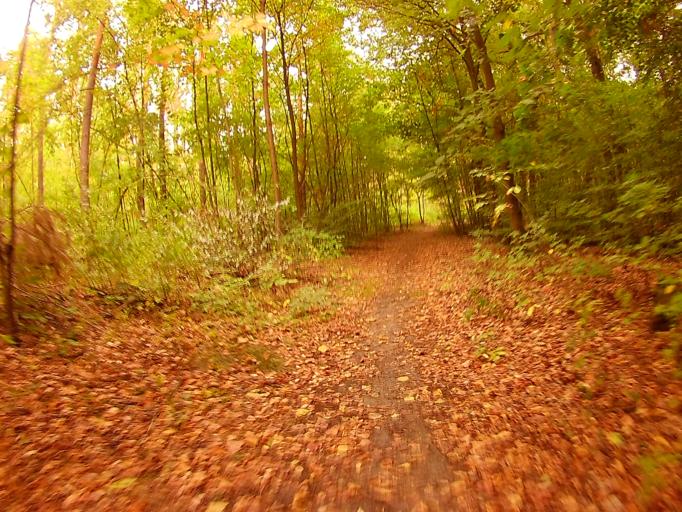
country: DE
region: Berlin
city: Grunau
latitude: 52.4071
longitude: 13.6030
